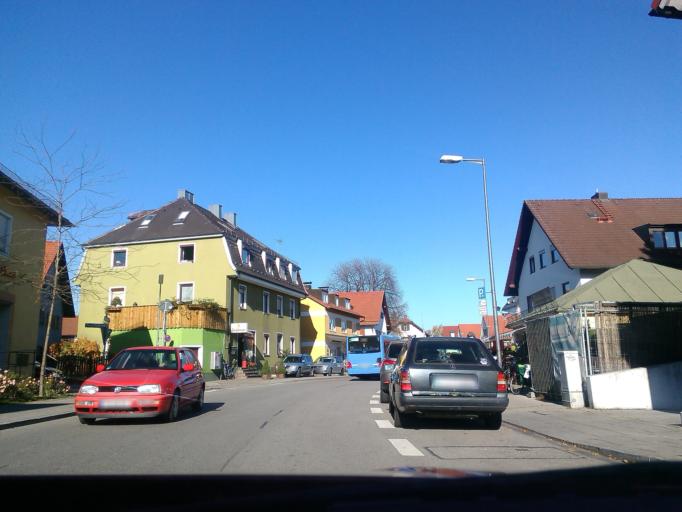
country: DE
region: Bavaria
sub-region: Upper Bavaria
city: Grafelfing
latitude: 48.1581
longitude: 11.4153
